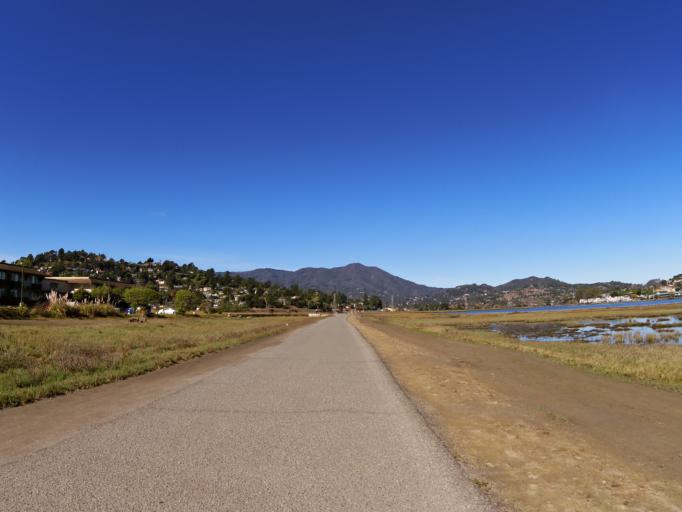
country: US
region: California
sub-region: Marin County
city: Marin City
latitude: 37.8818
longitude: -122.5177
